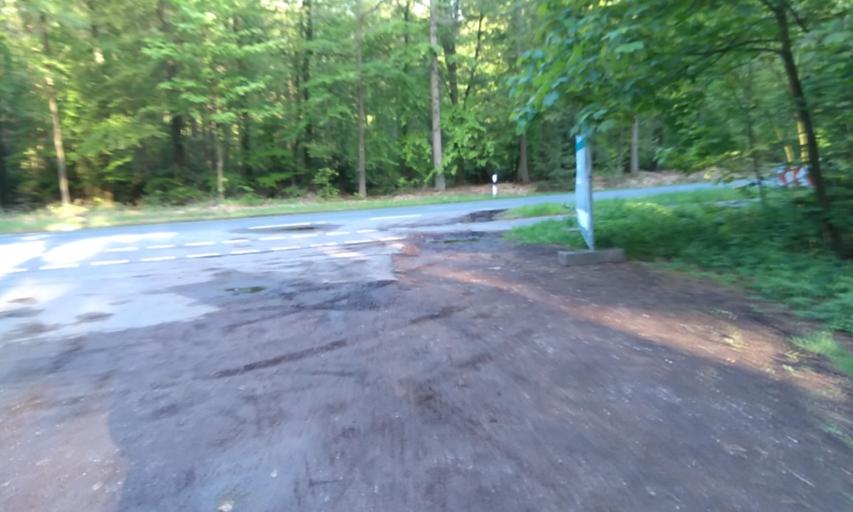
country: DE
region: Lower Saxony
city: Wohnste
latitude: 53.3980
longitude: 9.5387
